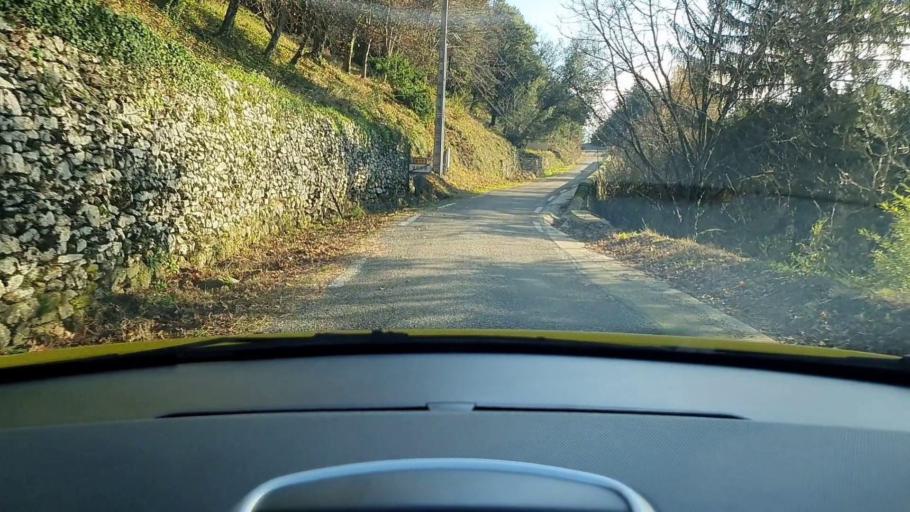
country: FR
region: Languedoc-Roussillon
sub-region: Departement du Gard
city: Branoux-les-Taillades
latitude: 44.3155
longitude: 3.9913
